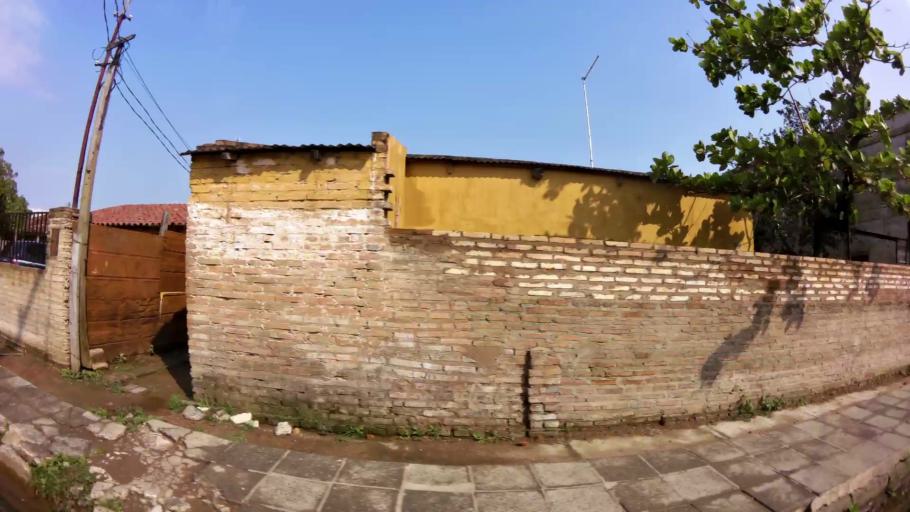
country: PY
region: Asuncion
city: Asuncion
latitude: -25.3132
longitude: -57.6679
